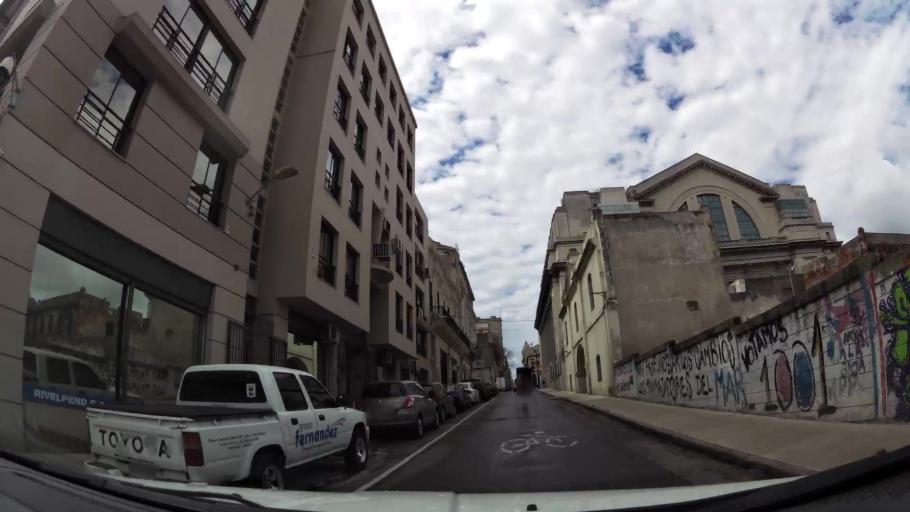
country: UY
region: Montevideo
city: Montevideo
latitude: -34.9043
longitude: -56.2087
